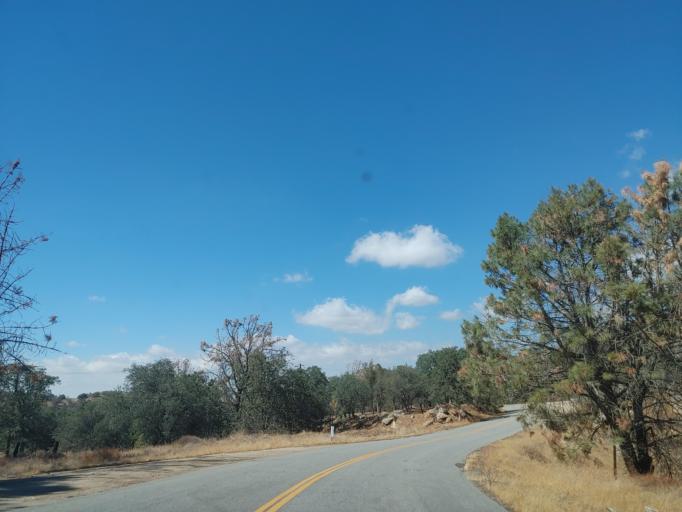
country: US
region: California
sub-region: Kern County
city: Golden Hills
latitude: 35.1990
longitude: -118.5409
